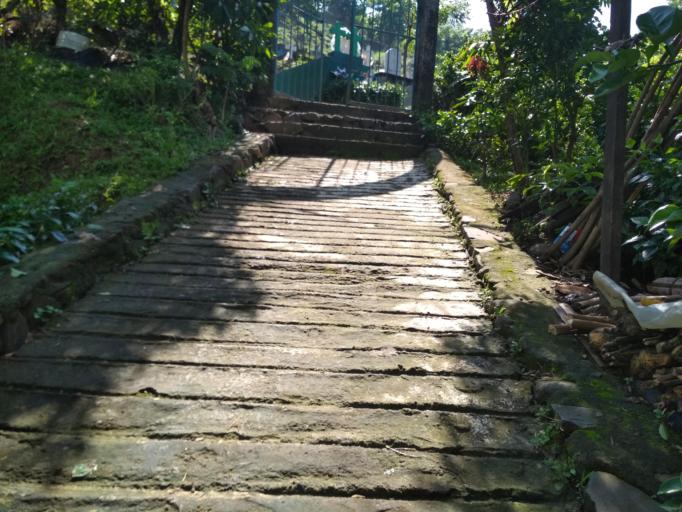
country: MX
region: Veracruz
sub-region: San Andres Tuxtla
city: Texcaltitan Xoteapan (Texcaltitan)
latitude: 18.4481
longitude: -95.2523
